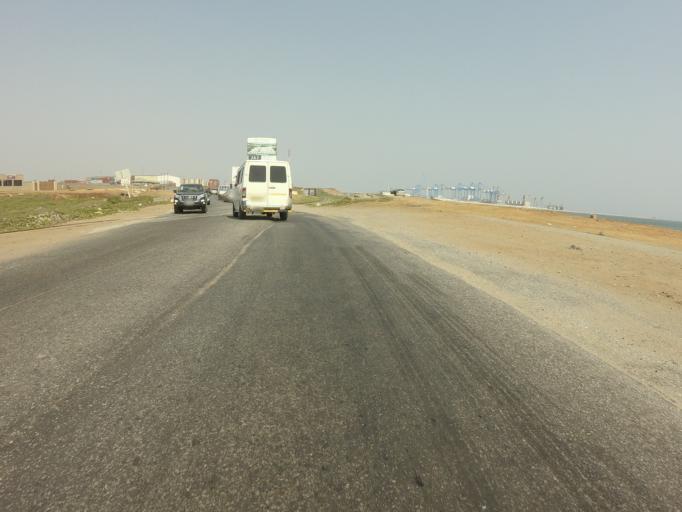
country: GH
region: Greater Accra
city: Nungua
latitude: 5.6138
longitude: -0.0287
